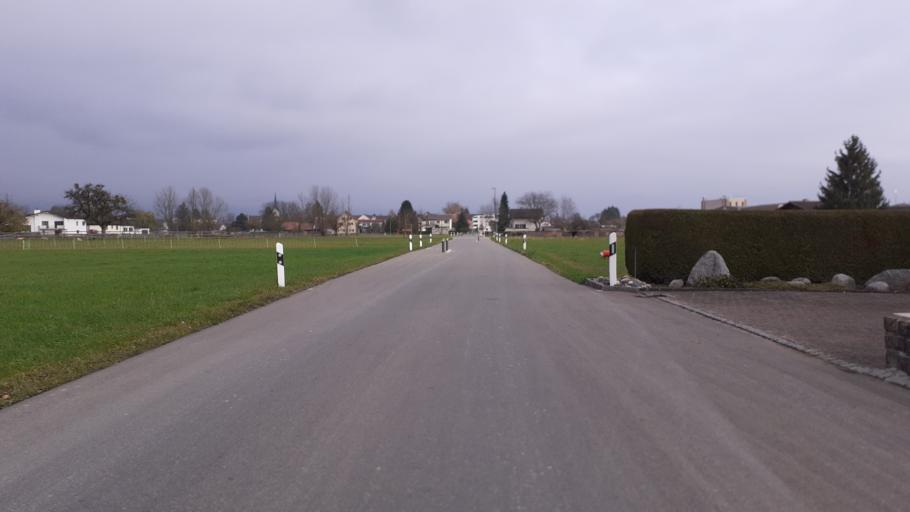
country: CH
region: Saint Gallen
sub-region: Wahlkreis Rheintal
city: Oberriet
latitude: 47.3102
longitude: 9.5653
